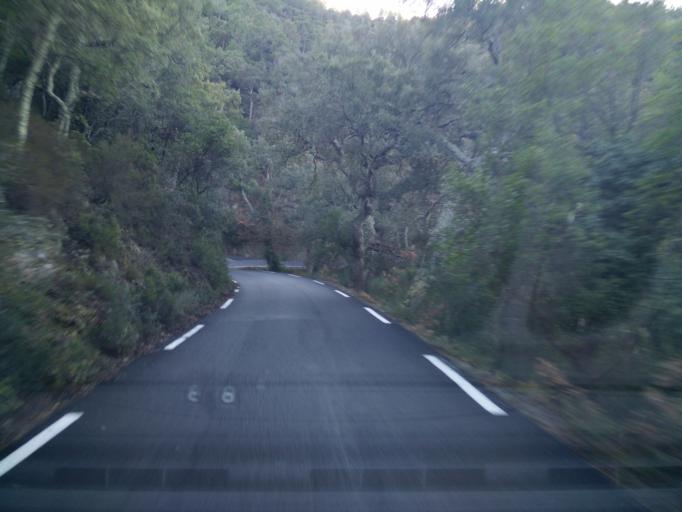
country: FR
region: Provence-Alpes-Cote d'Azur
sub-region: Departement du Var
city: Collobrieres
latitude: 43.2401
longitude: 6.3426
